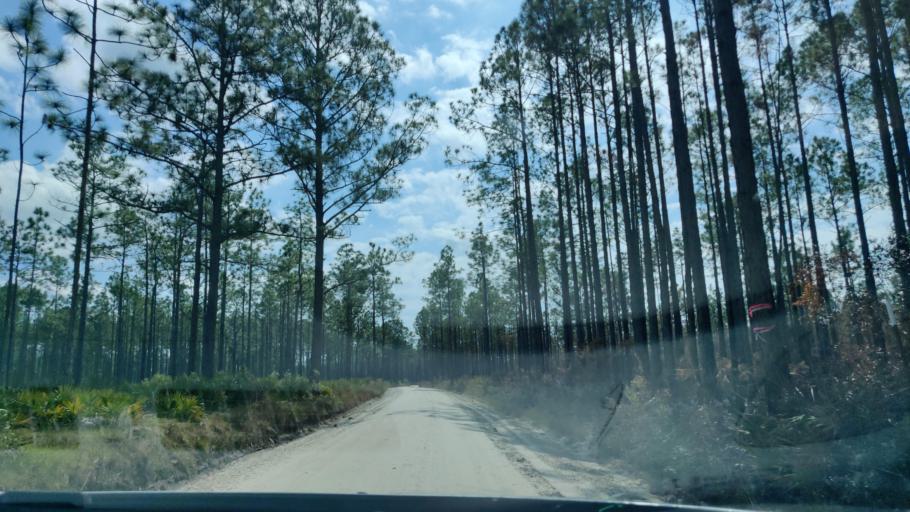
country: US
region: Florida
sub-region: Clay County
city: Middleburg
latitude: 30.1635
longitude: -81.9478
